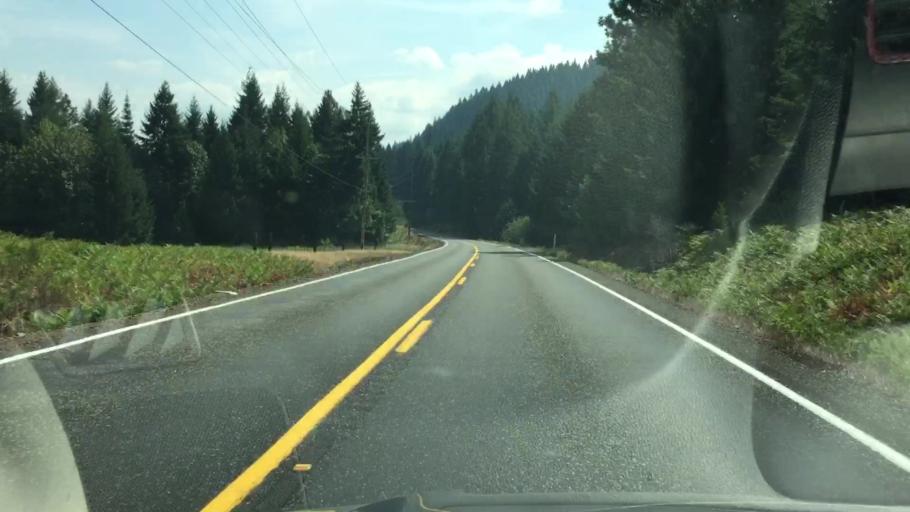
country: US
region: Washington
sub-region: Klickitat County
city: White Salmon
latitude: 45.8811
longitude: -121.5212
